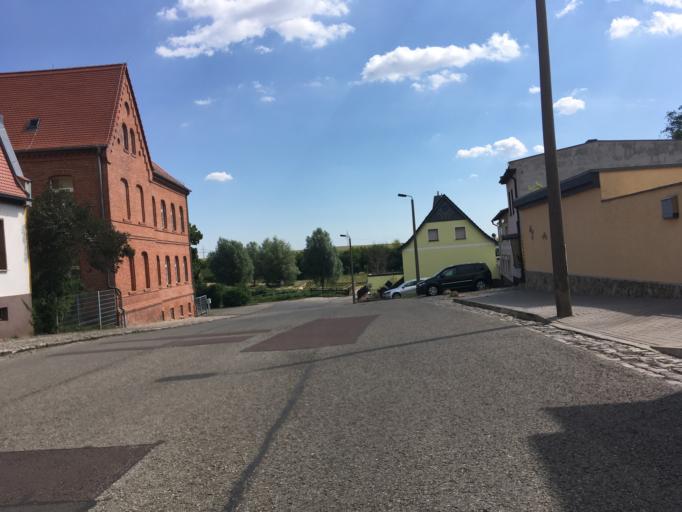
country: DE
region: Saxony-Anhalt
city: Bernburg
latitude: 51.7820
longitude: 11.7664
